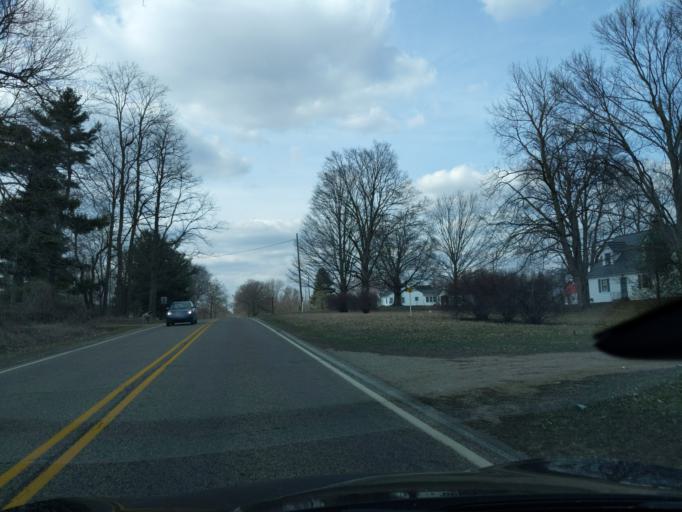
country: US
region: Michigan
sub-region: Jackson County
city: Jackson
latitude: 42.3136
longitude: -84.4136
